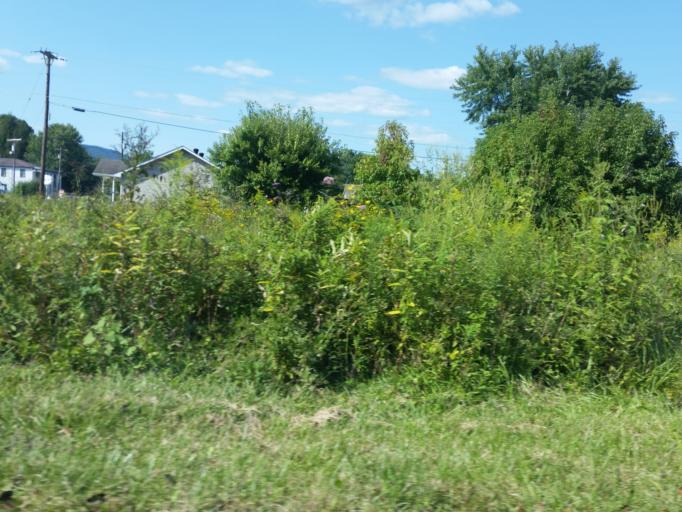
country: US
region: Kentucky
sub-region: Bell County
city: Middlesboro
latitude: 36.6016
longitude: -83.7290
